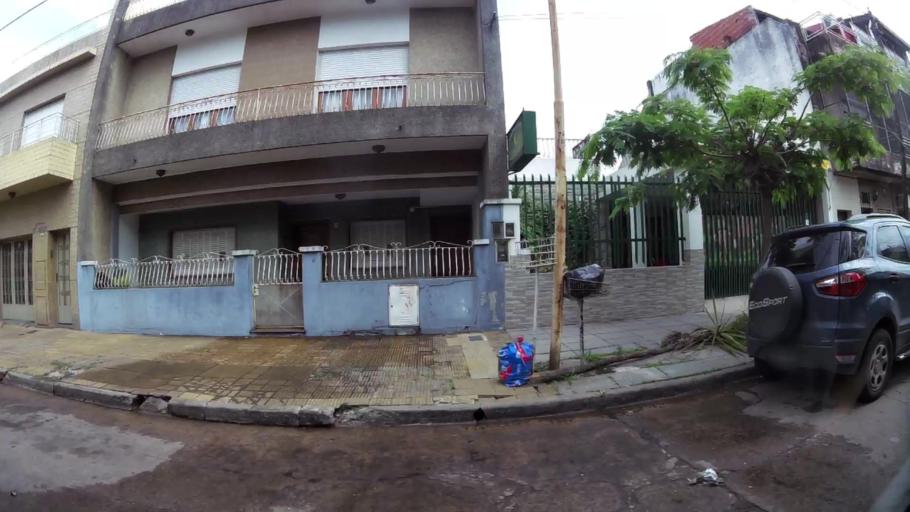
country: AR
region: Buenos Aires F.D.
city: Villa Lugano
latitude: -34.6833
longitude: -58.4982
